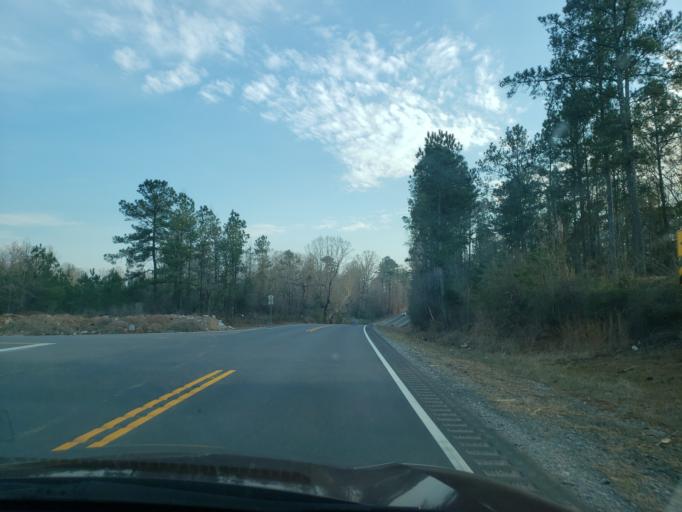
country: US
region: Alabama
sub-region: Hale County
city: Moundville
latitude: 32.8834
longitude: -87.6083
